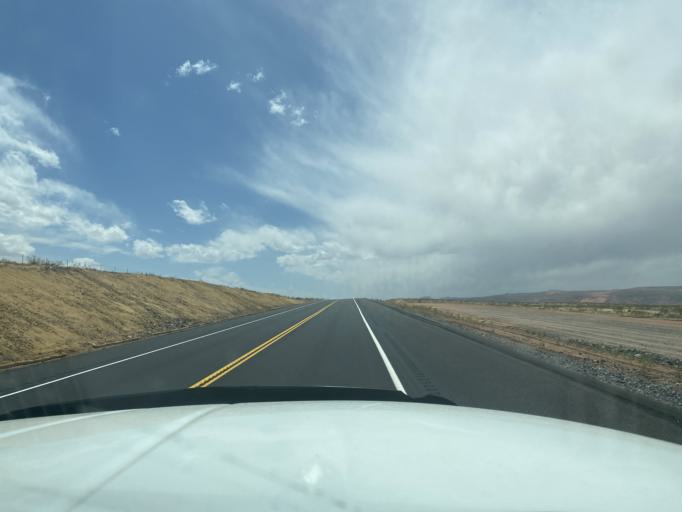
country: US
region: Utah
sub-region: Washington County
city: Hurricane
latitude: 37.1605
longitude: -113.3459
